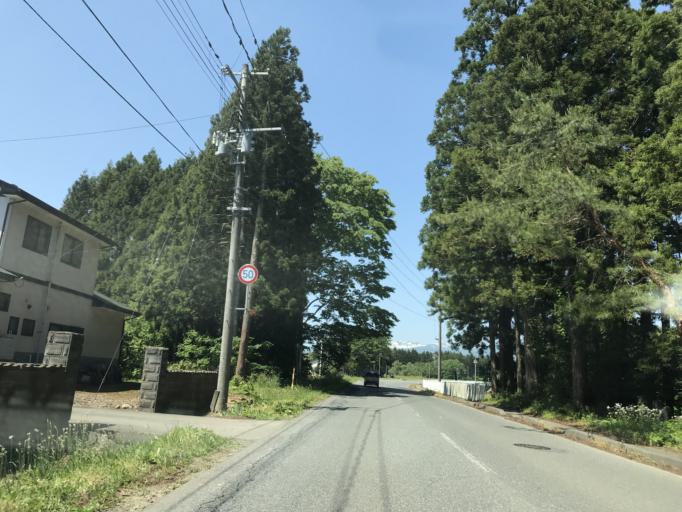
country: JP
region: Iwate
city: Mizusawa
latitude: 39.1953
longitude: 141.0800
